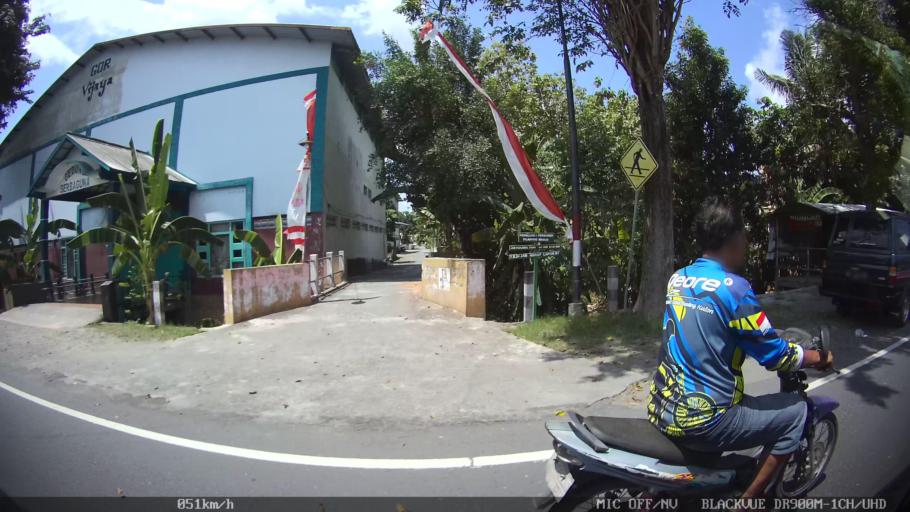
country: ID
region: Daerah Istimewa Yogyakarta
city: Sewon
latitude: -7.8869
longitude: 110.3464
